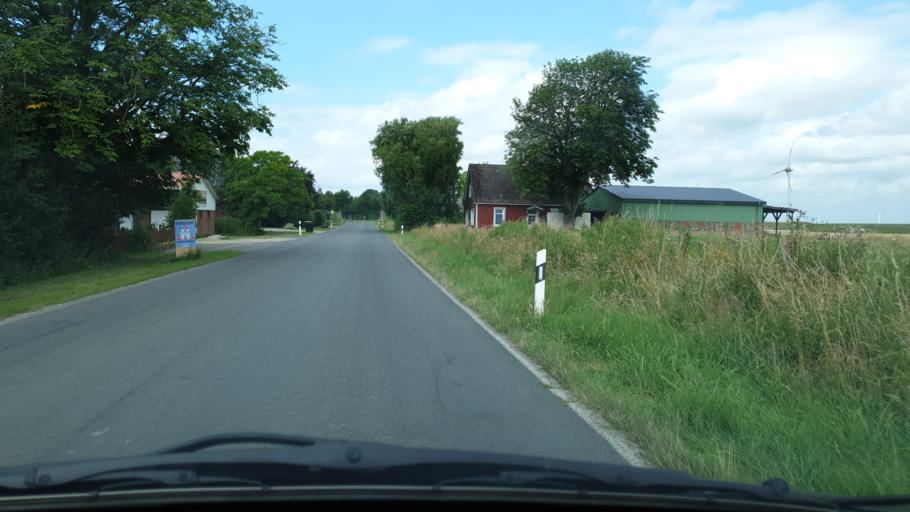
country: DE
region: Schleswig-Holstein
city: Kronprinzenkoog
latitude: 53.9532
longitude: 8.9369
